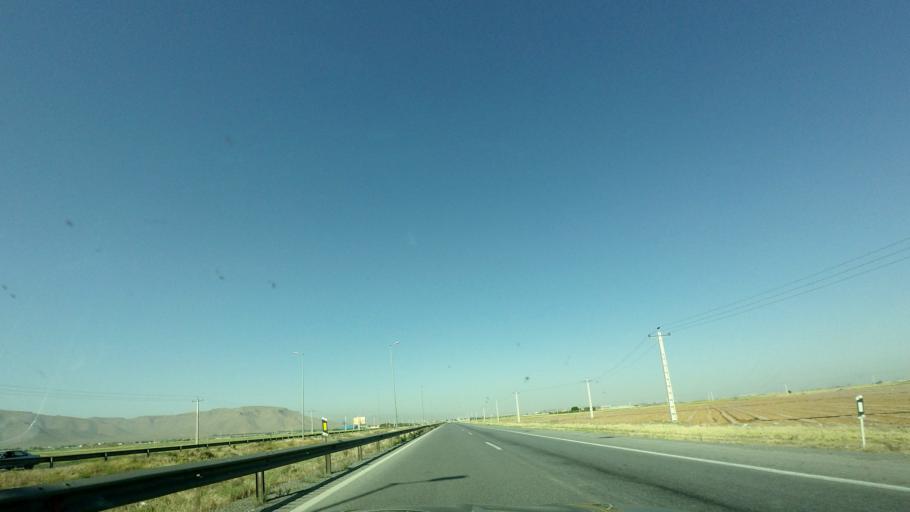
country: IR
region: Markazi
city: Arak
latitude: 34.1600
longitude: 50.0136
